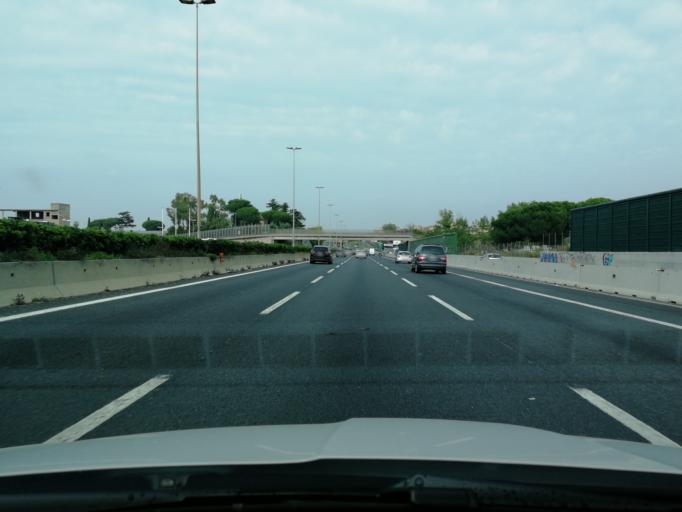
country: IT
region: Latium
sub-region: Citta metropolitana di Roma Capitale
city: Setteville
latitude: 41.8841
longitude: 12.6122
